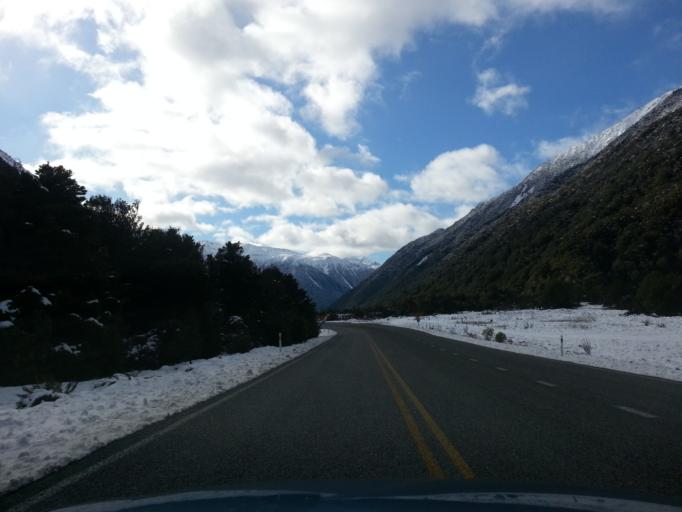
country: NZ
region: West Coast
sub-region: Grey District
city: Greymouth
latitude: -42.8537
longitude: 171.5606
